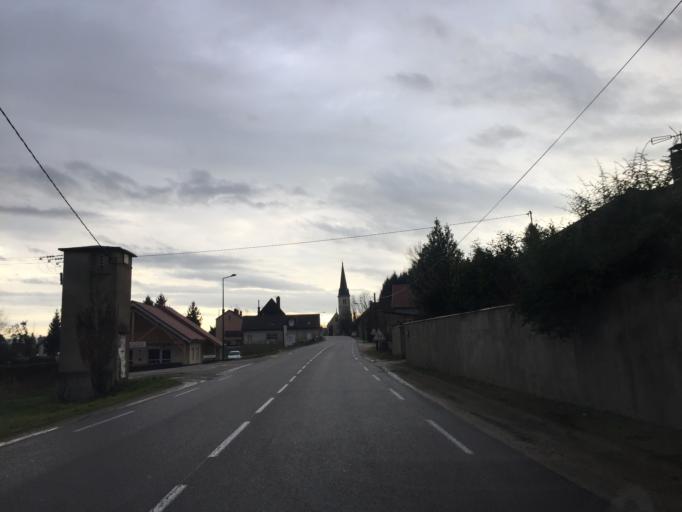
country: FR
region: Franche-Comte
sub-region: Departement du Jura
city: Mont-sous-Vaudrey
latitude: 46.9952
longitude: 5.5479
